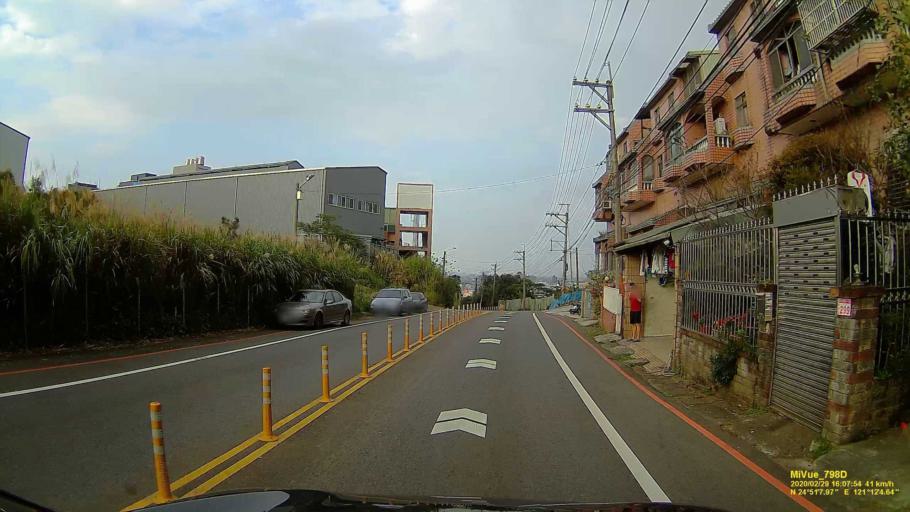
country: TW
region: Taiwan
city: Daxi
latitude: 24.8523
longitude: 121.2014
